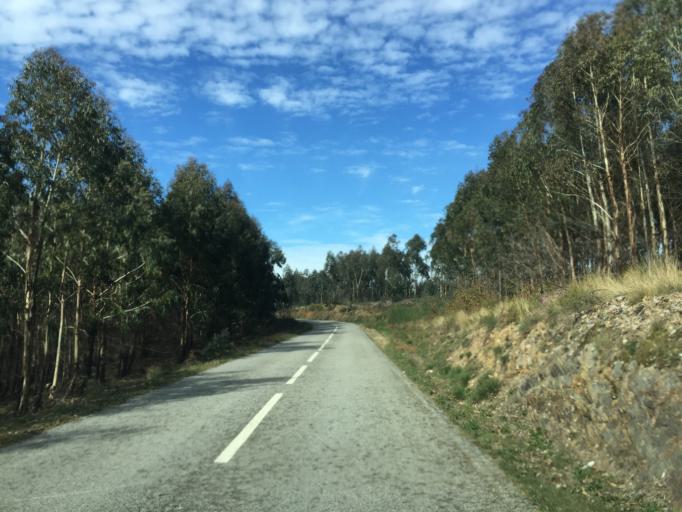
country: PT
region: Aveiro
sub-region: Arouca
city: Arouca
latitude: 40.9606
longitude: -8.2347
